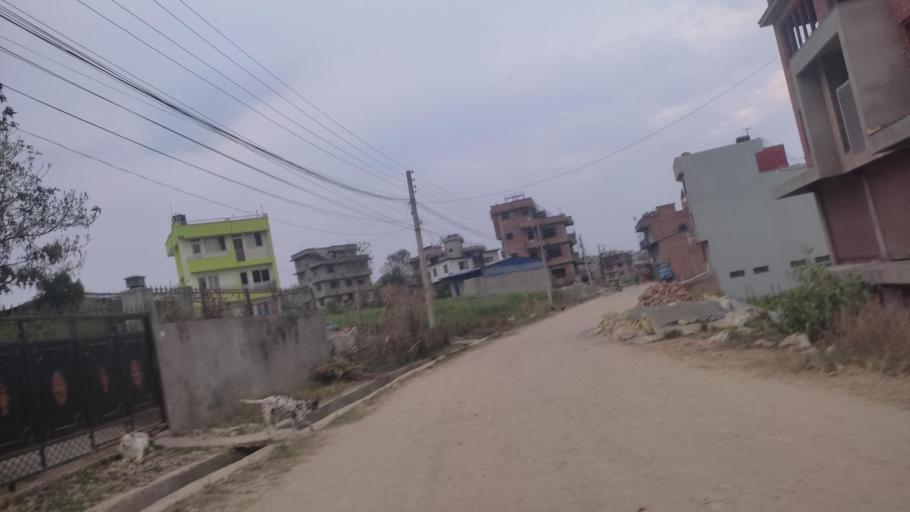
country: NP
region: Central Region
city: Kirtipur
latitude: 27.6659
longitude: 85.2768
